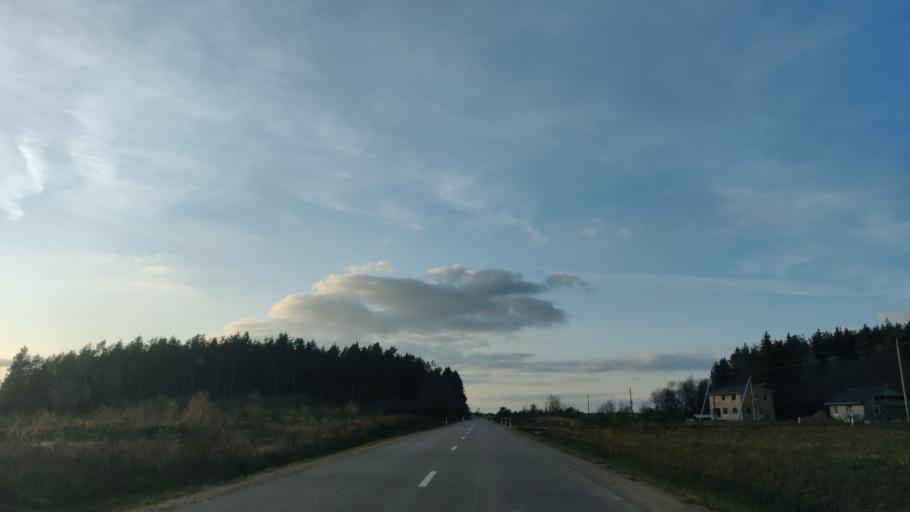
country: LT
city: Lentvaris
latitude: 54.5976
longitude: 25.0289
